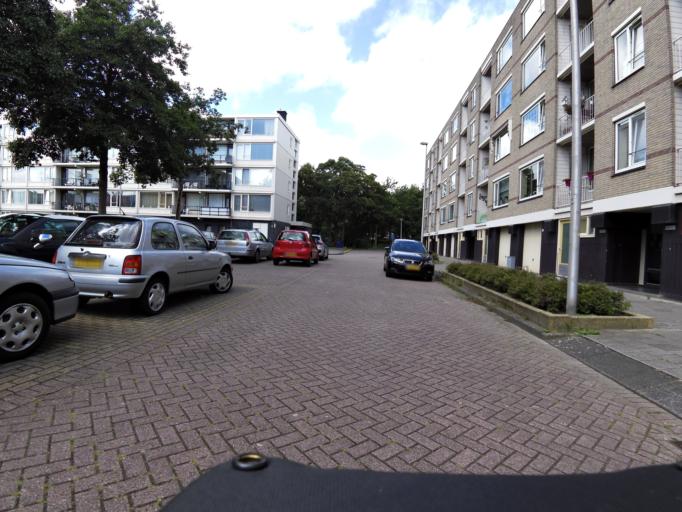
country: NL
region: South Holland
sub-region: Gemeente Spijkenisse
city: Spijkenisse
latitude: 51.8423
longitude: 4.3273
